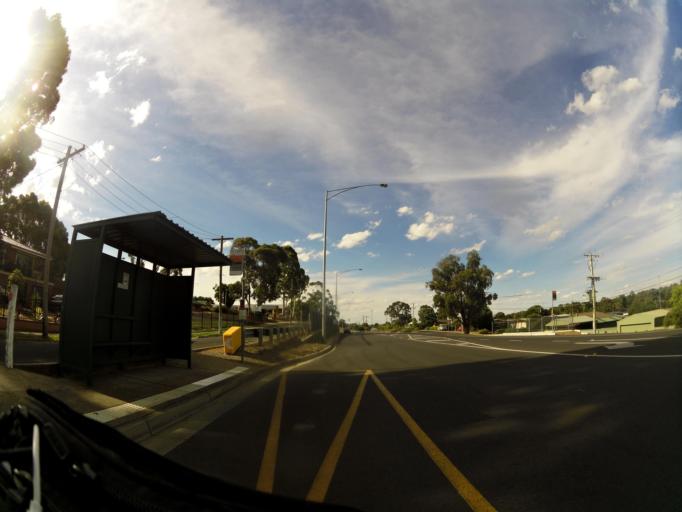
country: AU
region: Victoria
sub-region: Ballarat North
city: Mount Clear
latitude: -37.6054
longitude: 143.8689
